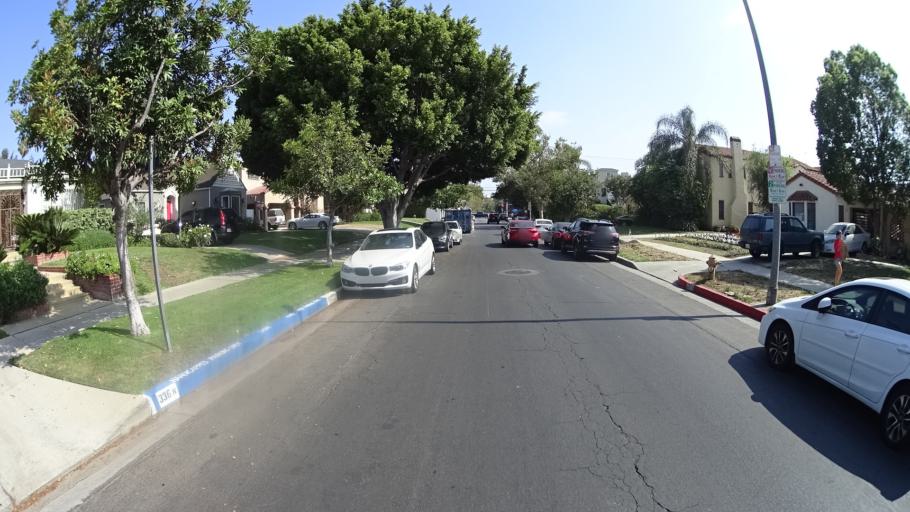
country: US
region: California
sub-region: Los Angeles County
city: West Hollywood
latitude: 34.0773
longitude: -118.3511
